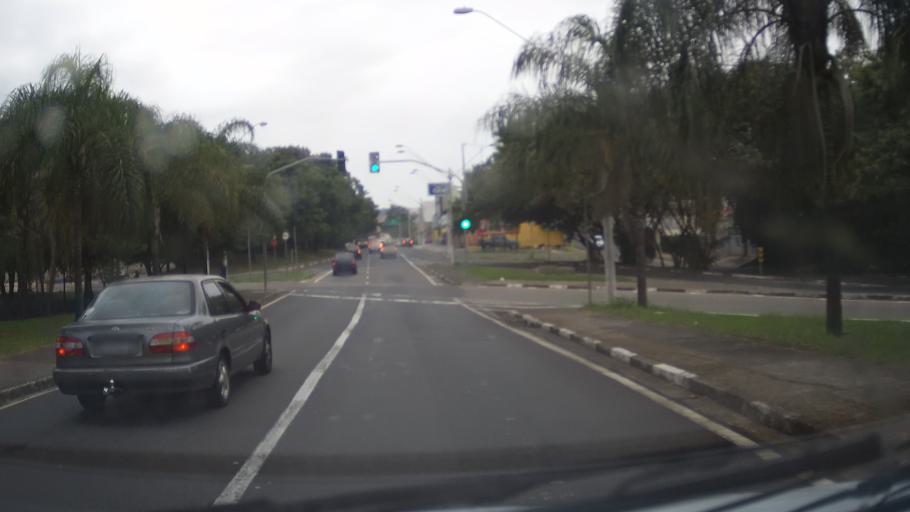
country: BR
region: Sao Paulo
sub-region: Campinas
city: Campinas
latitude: -22.9291
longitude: -47.0576
